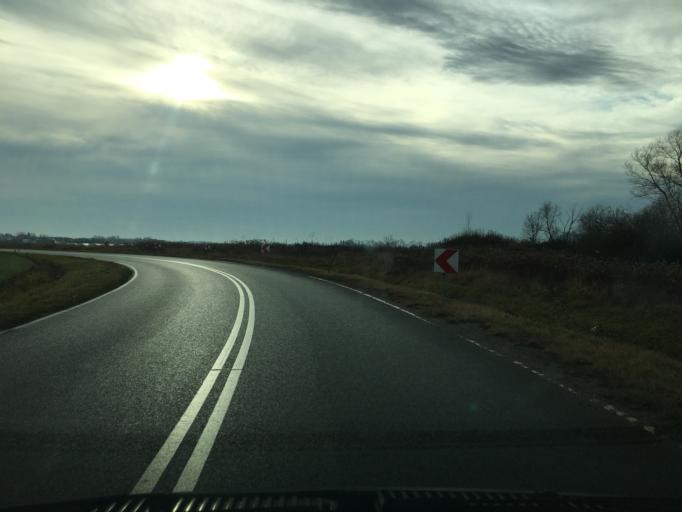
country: PL
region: Lower Silesian Voivodeship
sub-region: Powiat wroclawski
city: Dlugoleka
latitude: 51.1752
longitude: 17.2207
